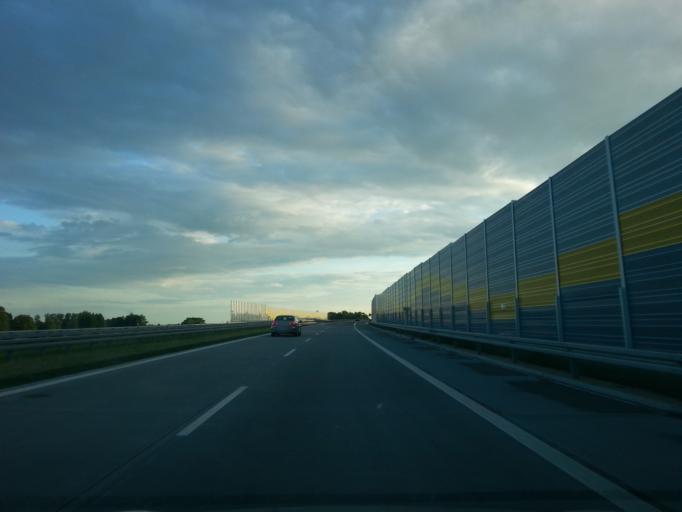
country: PL
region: Lodz Voivodeship
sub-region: Powiat wieruszowski
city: Lututow
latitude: 51.3213
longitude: 18.4336
